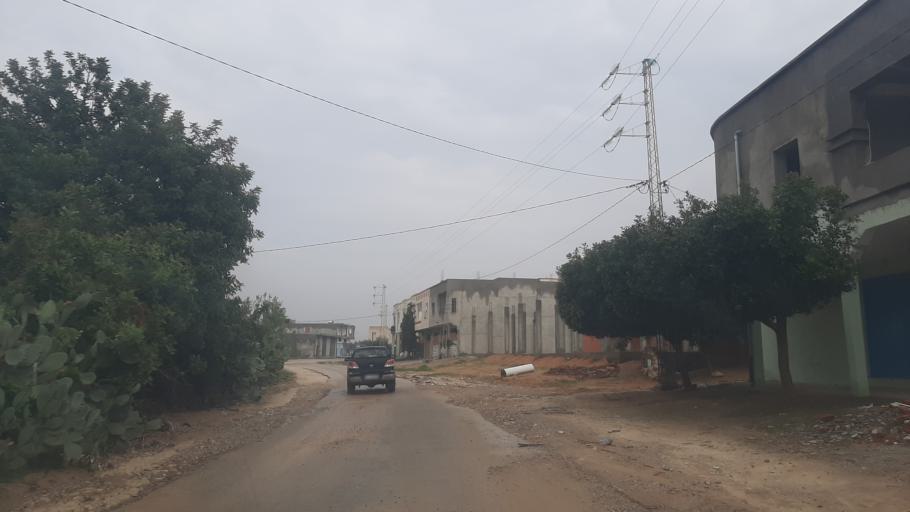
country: TN
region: Al Munastir
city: Sidi Bin Nur
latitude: 35.4773
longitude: 10.8747
